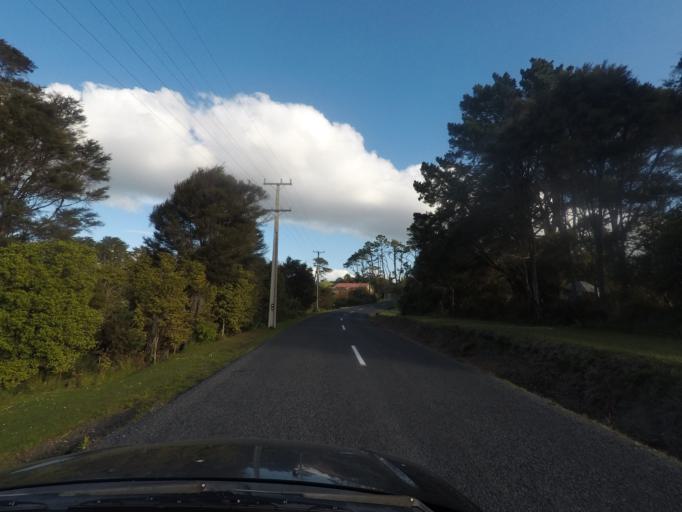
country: NZ
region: Auckland
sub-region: Auckland
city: Waitakere
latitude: -36.9185
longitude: 174.6154
